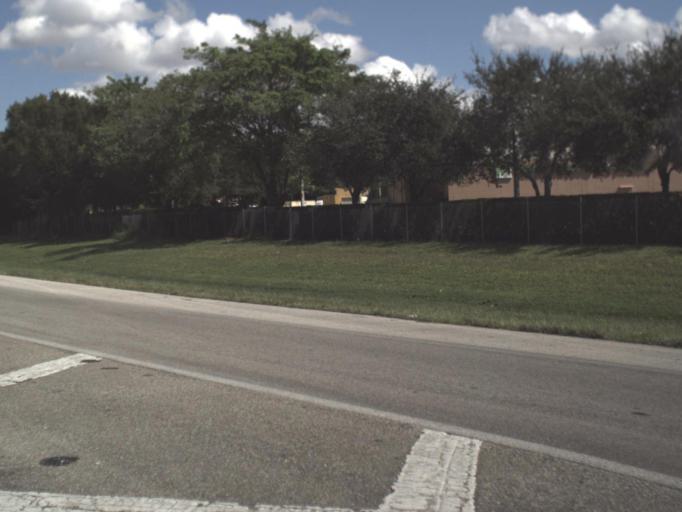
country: US
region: Florida
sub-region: Miami-Dade County
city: The Crossings
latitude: 25.6906
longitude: -80.3889
